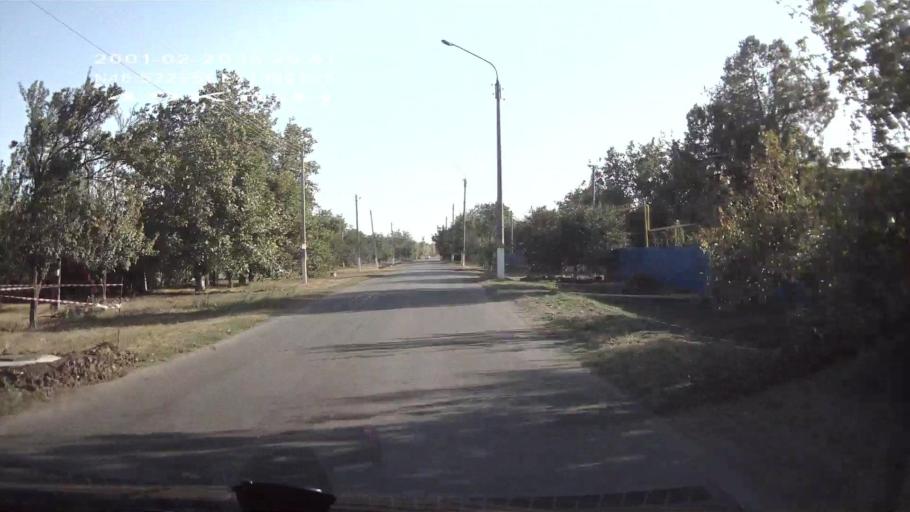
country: RU
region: Rostov
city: Gigant
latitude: 46.5224
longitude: 41.1908
